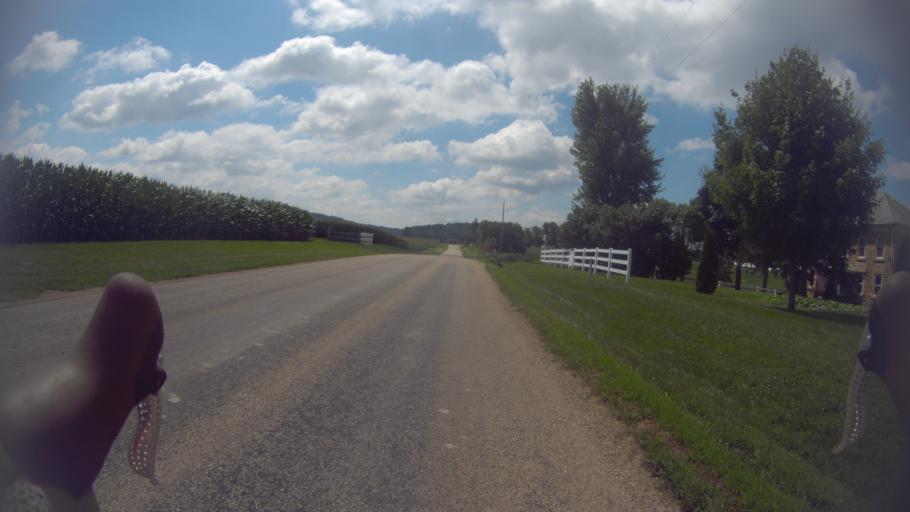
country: US
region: Wisconsin
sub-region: Sauk County
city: Sauk City
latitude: 43.2244
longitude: -89.6404
